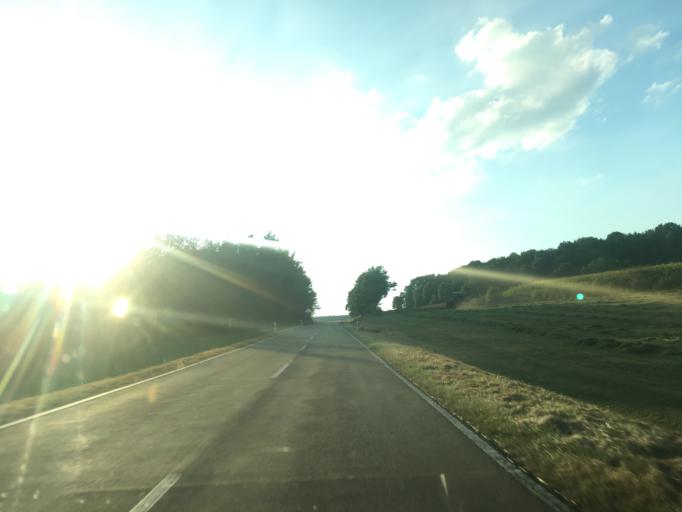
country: DE
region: Baden-Wuerttemberg
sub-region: Tuebingen Region
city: Rechtenstein
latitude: 48.2531
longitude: 9.5289
